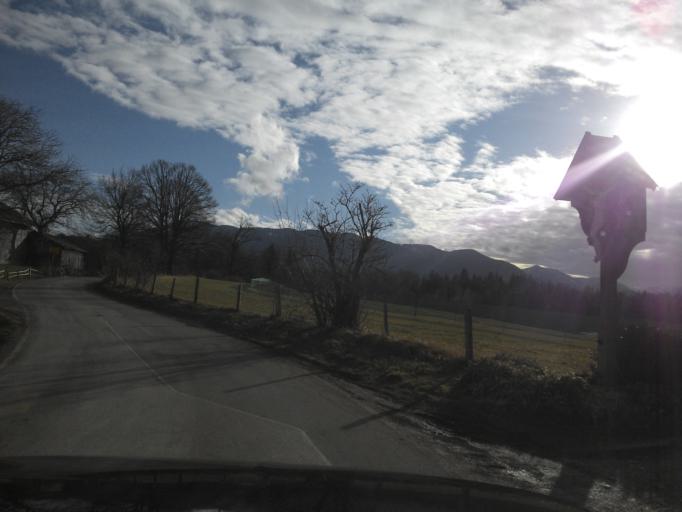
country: DE
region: Bavaria
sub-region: Upper Bavaria
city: Kreut
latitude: 47.7984
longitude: 11.4832
